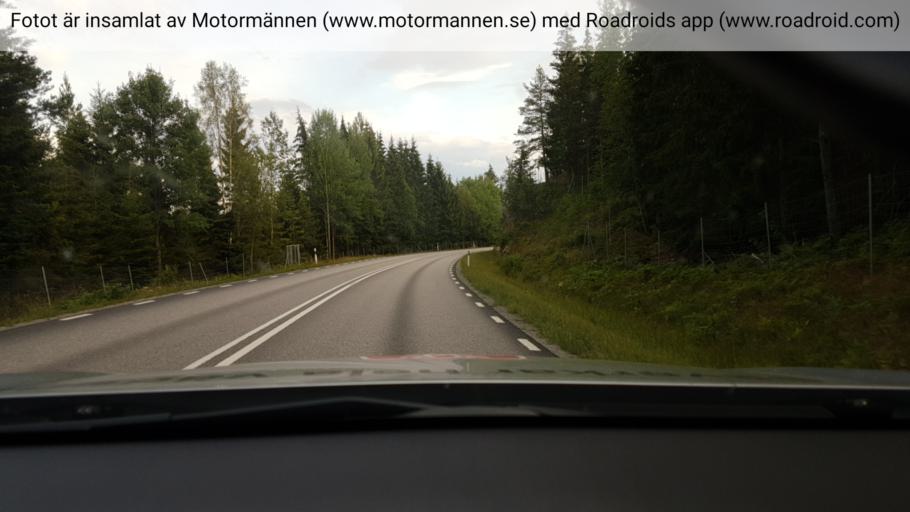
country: SE
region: Vaestra Goetaland
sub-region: Fargelanda Kommun
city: Faergelanda
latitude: 58.4688
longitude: 12.0194
